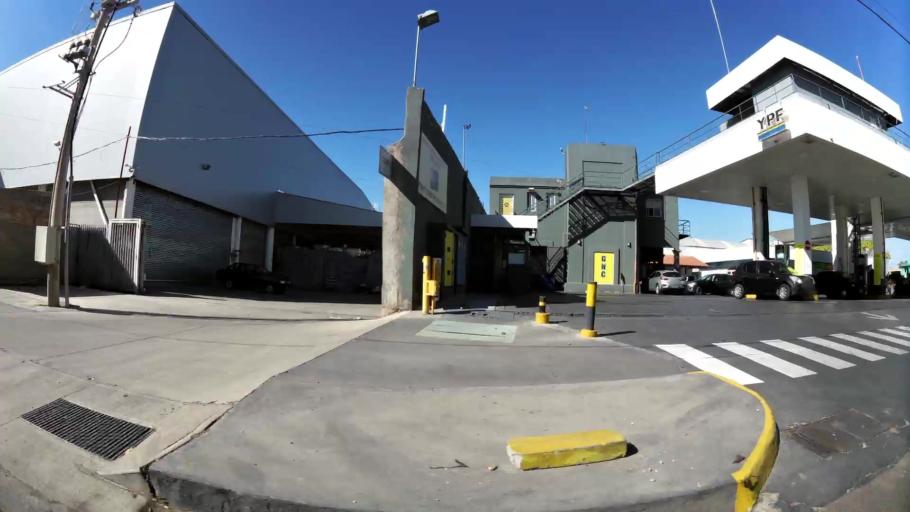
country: AR
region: Mendoza
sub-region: Departamento de Godoy Cruz
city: Godoy Cruz
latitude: -32.9256
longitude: -68.8363
